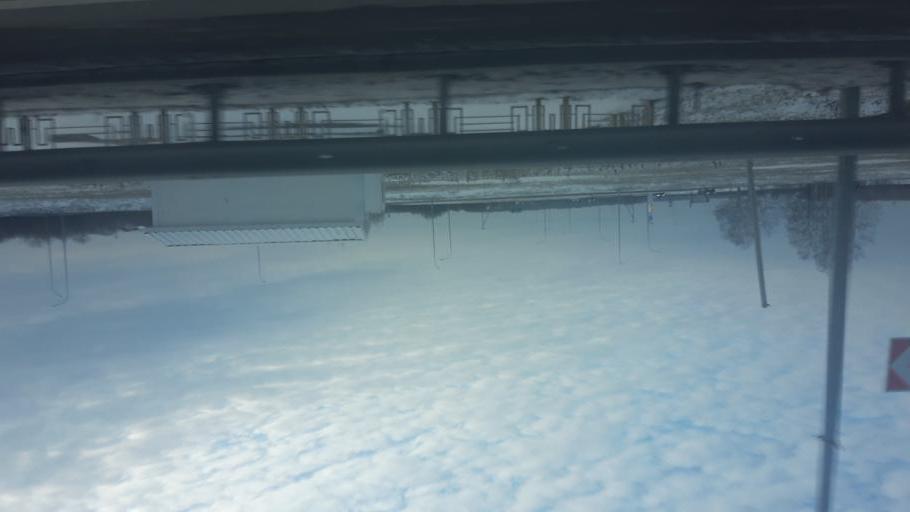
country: RU
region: Tjumen
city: Moskovskiy
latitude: 57.1868
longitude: 65.3576
